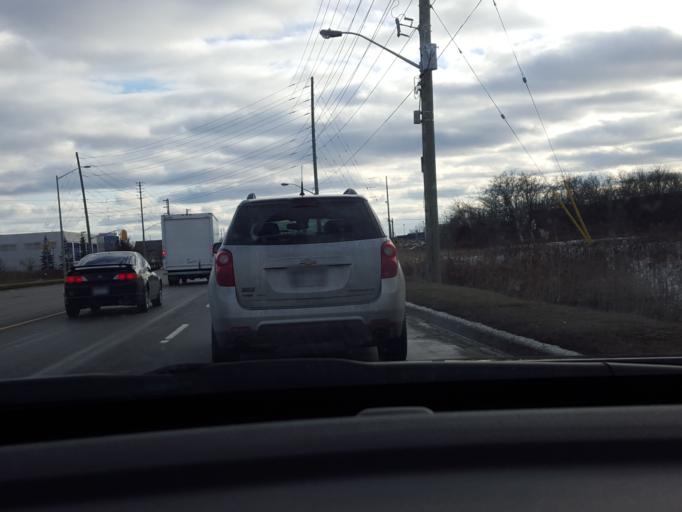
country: CA
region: Ontario
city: Ajax
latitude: 43.8683
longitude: -79.0181
